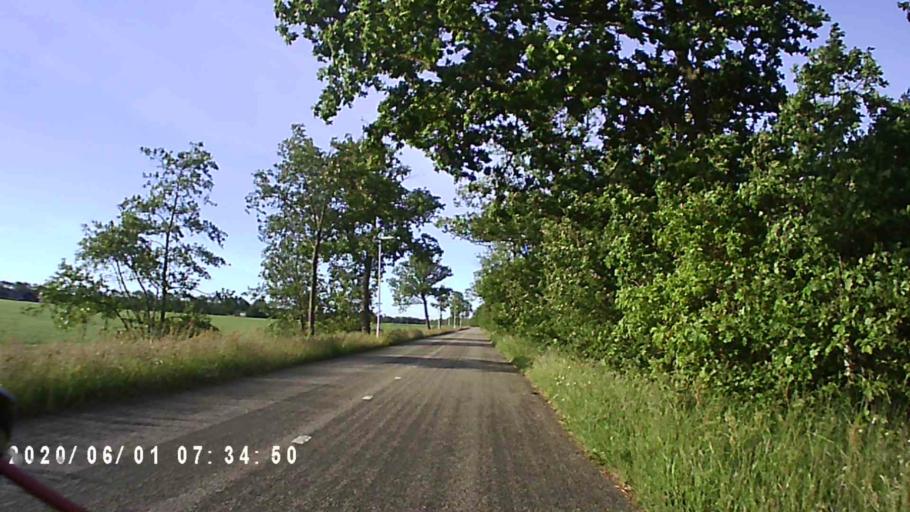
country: NL
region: Friesland
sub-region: Gemeente Dongeradeel
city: Dokkum
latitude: 53.3086
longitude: 5.9943
